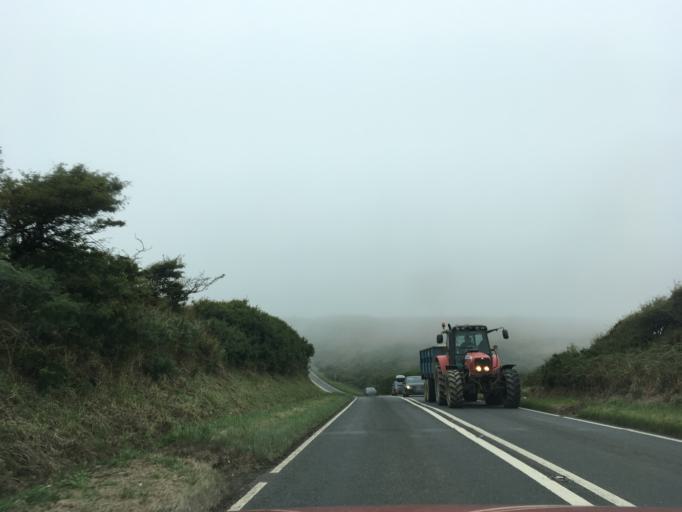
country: GB
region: Wales
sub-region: Pembrokeshire
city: Saint David's
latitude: 51.8800
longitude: -5.2402
